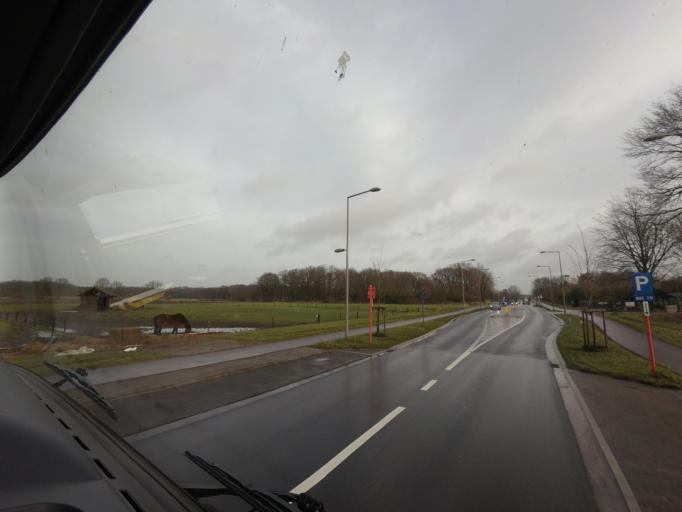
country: BE
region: Flanders
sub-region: Provincie Antwerpen
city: Stabroek
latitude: 51.3422
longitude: 4.3872
